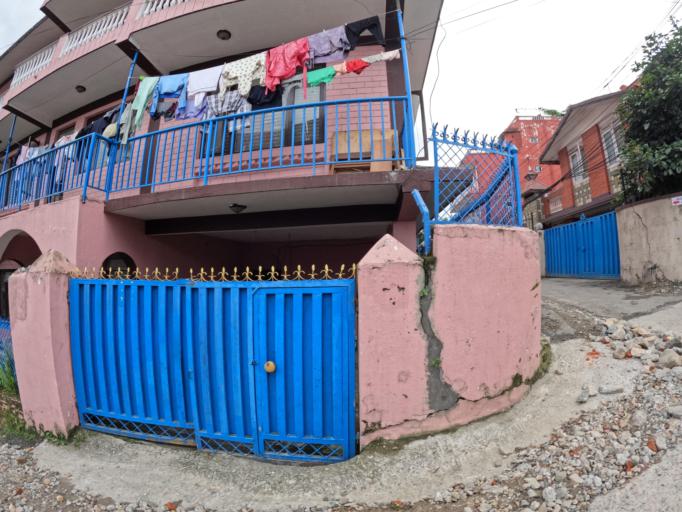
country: NP
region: Central Region
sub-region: Bagmati Zone
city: Kathmandu
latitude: 27.7411
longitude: 85.3201
